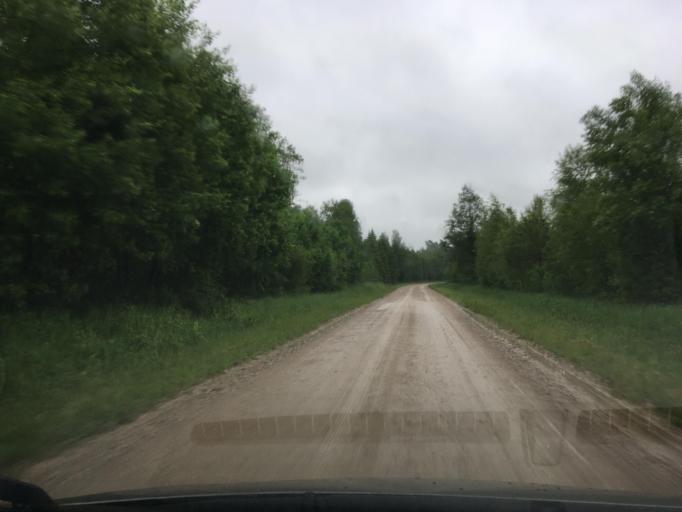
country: EE
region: Laeaene
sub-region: Lihula vald
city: Lihula
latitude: 58.6327
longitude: 23.8043
